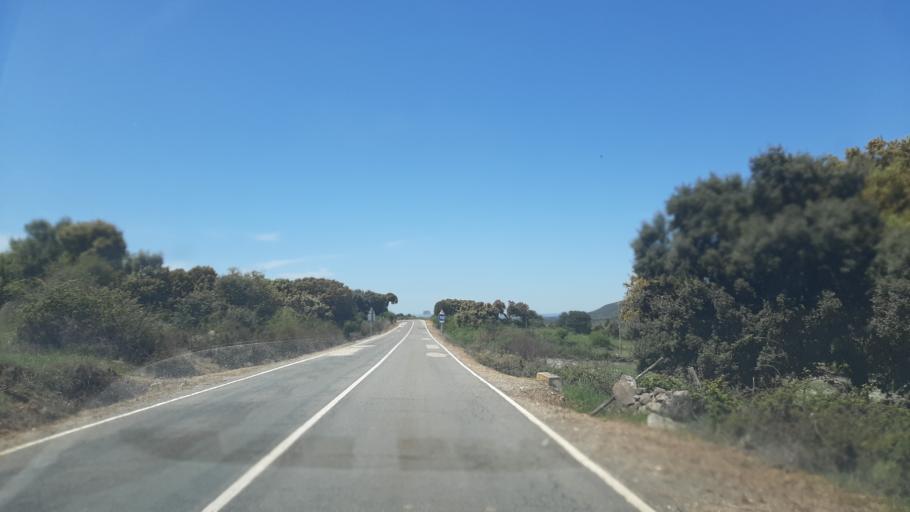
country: ES
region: Castille and Leon
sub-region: Provincia de Avila
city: Narrillos del Alamo
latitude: 40.5345
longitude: -5.4529
